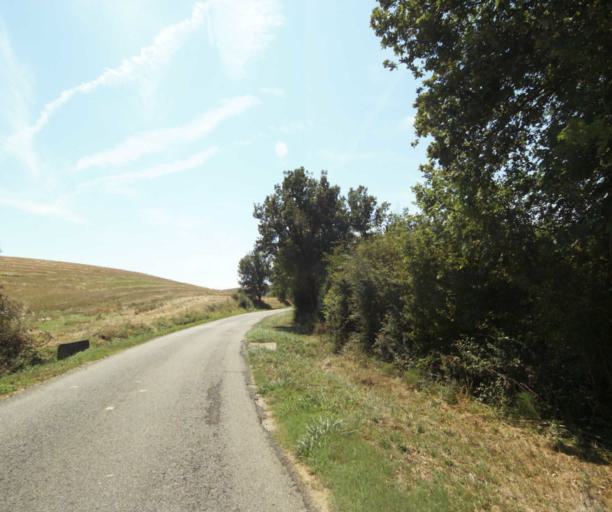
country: FR
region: Midi-Pyrenees
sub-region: Departement de l'Ariege
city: Lezat-sur-Leze
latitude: 43.2674
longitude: 1.3351
